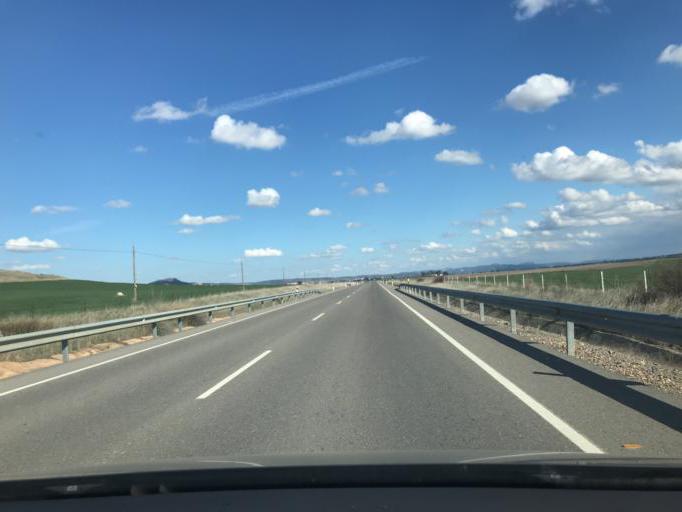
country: ES
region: Andalusia
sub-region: Province of Cordoba
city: Fuente Obejuna
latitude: 38.2823
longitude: -5.3724
